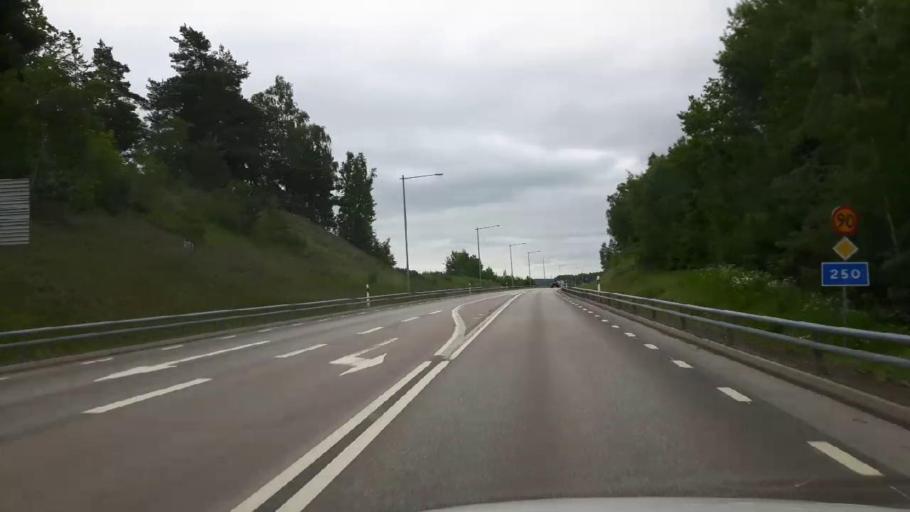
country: SE
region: Vaestmanland
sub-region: Kopings Kommun
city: Koping
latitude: 59.5511
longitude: 15.9106
